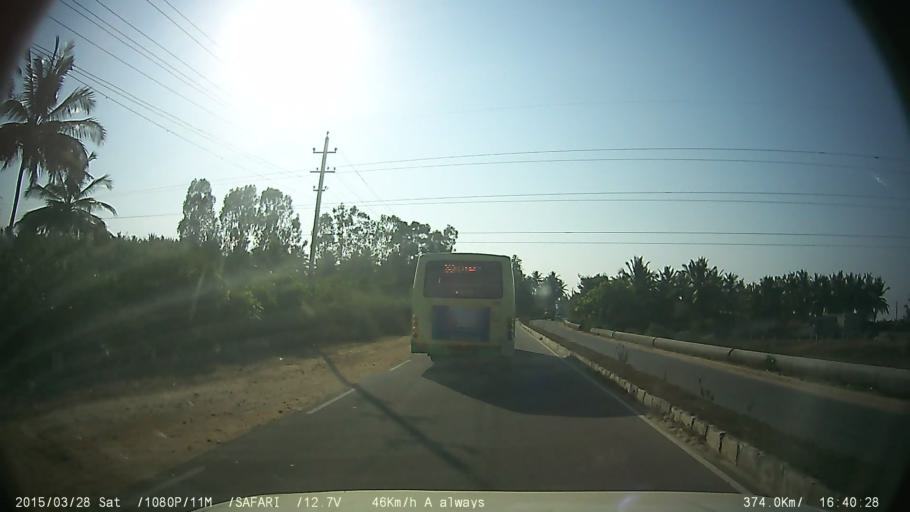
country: IN
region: Karnataka
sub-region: Mandya
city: Shrirangapattana
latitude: 12.3940
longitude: 76.5856
